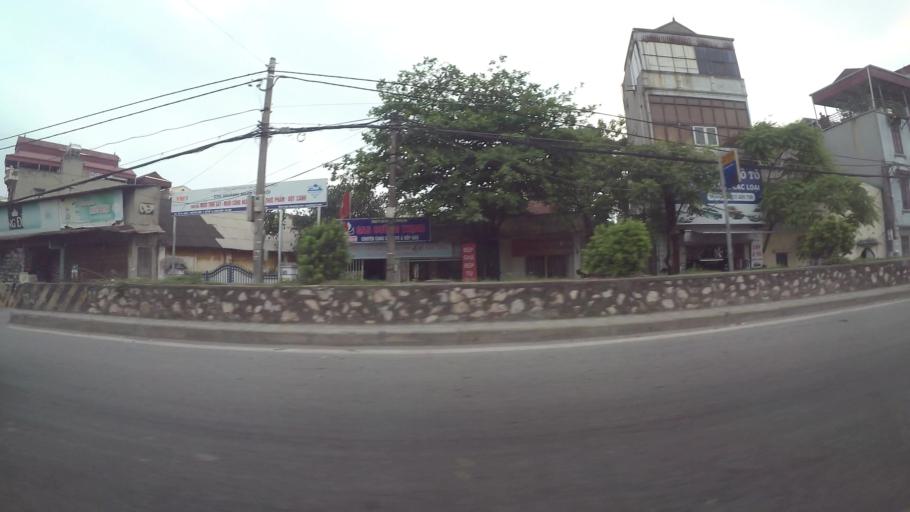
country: VN
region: Ha Noi
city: Hoan Kiem
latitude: 21.0385
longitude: 105.8678
